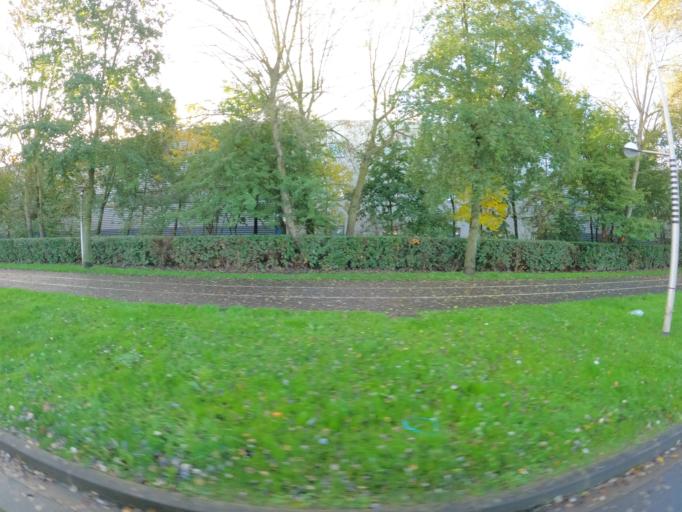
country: FR
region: Ile-de-France
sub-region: Departement de Seine-et-Marne
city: Ferrieres-en-Brie
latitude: 48.8340
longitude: 2.7139
